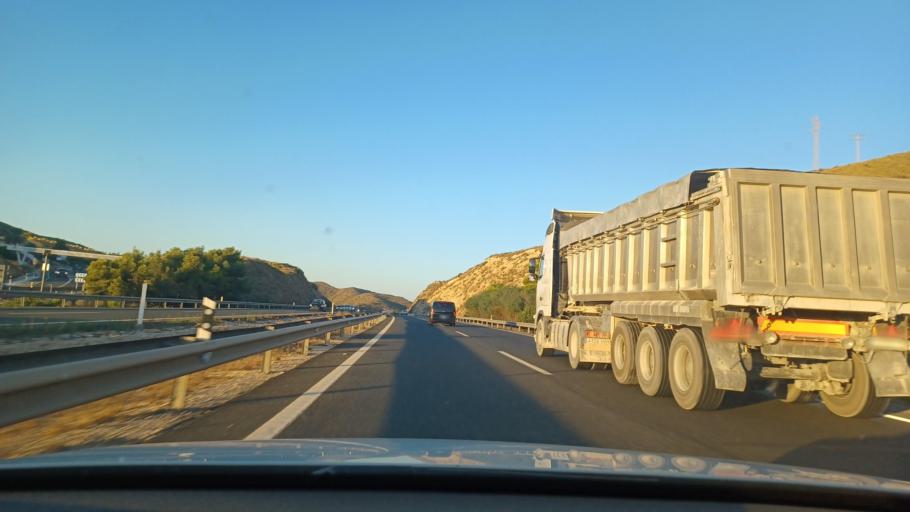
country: ES
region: Valencia
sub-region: Provincia de Alicante
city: Aiguees
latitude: 38.4719
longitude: -0.3367
